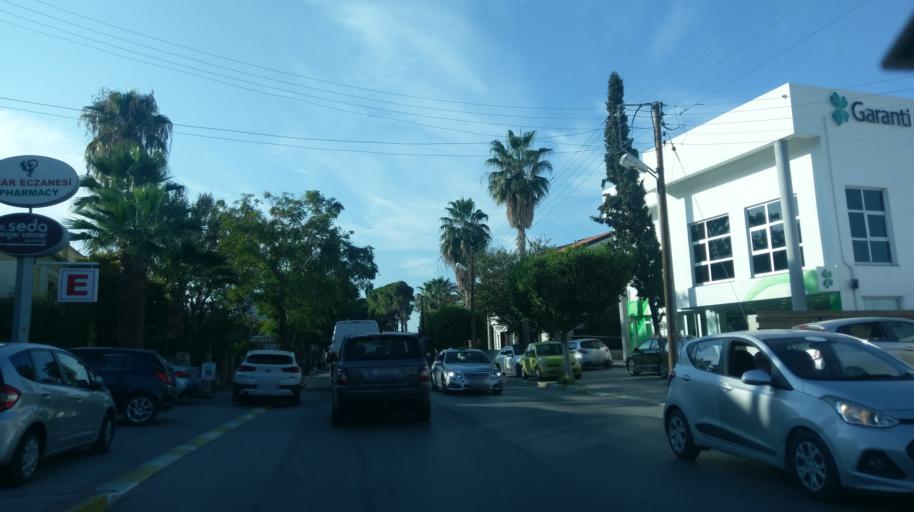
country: CY
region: Keryneia
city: Kyrenia
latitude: 35.3387
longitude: 33.3234
